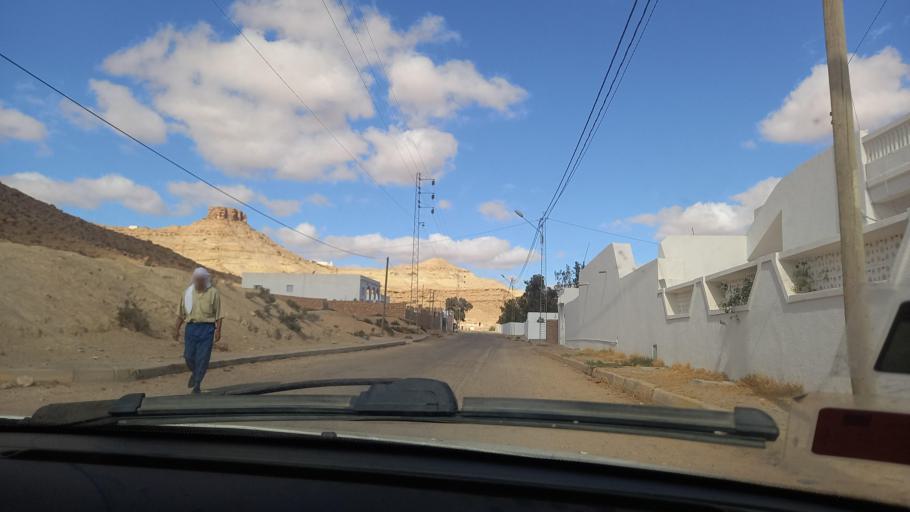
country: TN
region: Tataouine
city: Tataouine
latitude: 32.9828
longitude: 10.2629
